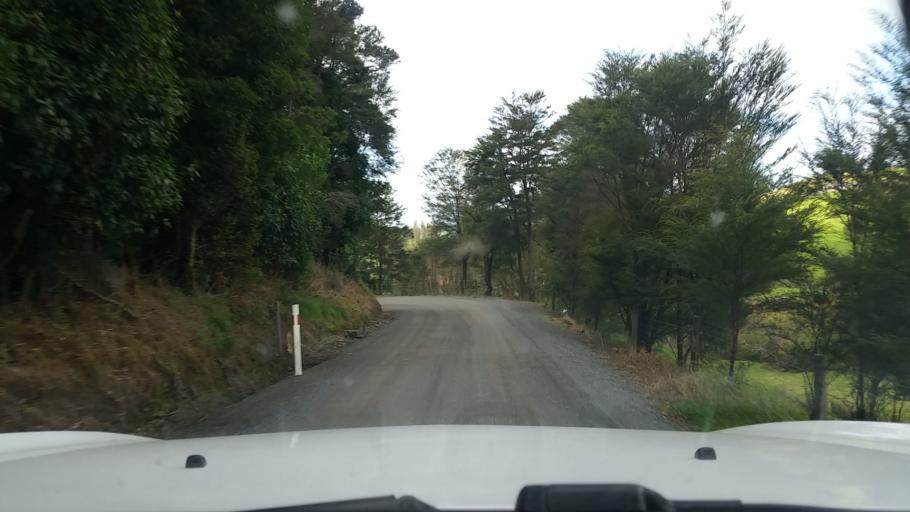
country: NZ
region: Waikato
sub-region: Hauraki District
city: Ngatea
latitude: -37.4472
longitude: 175.4844
